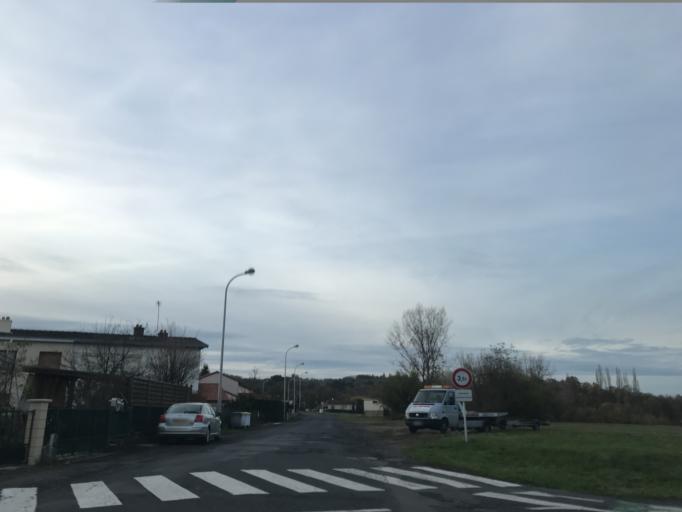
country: FR
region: Auvergne
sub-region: Departement du Puy-de-Dome
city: Courpiere
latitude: 45.7609
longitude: 3.5369
